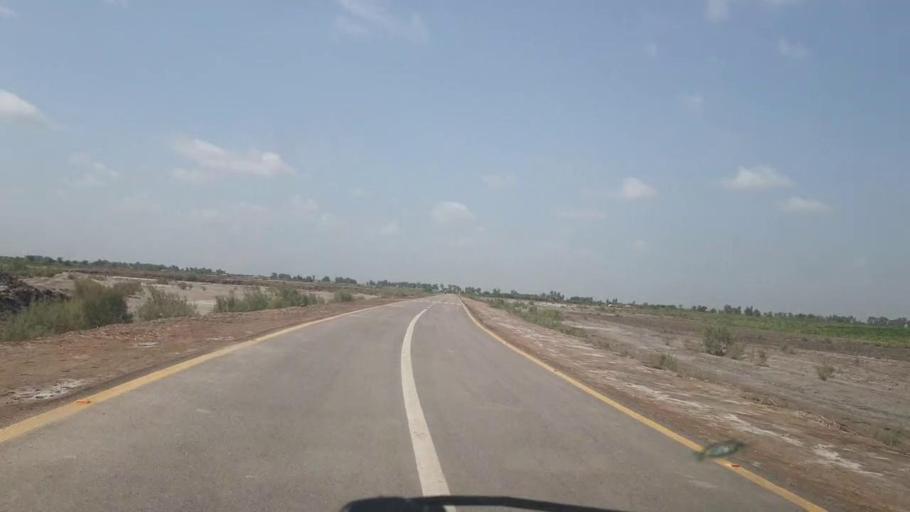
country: PK
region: Sindh
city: Berani
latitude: 25.7149
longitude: 68.9450
